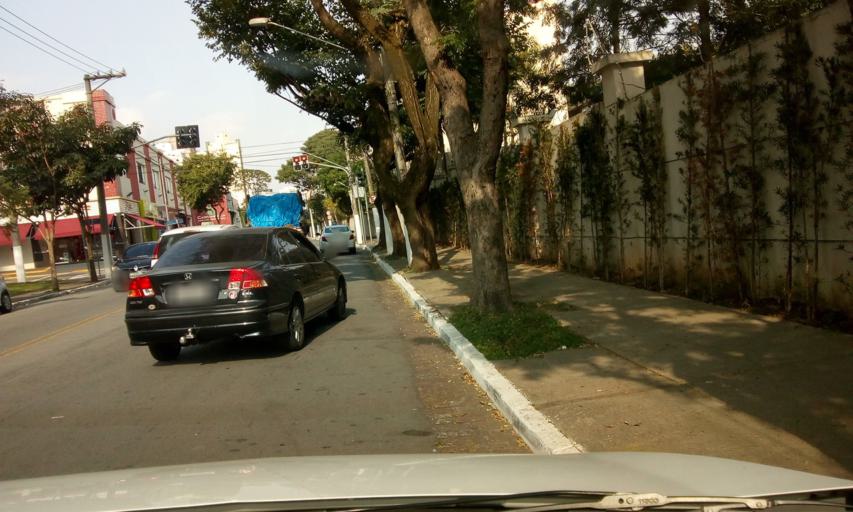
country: BR
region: Sao Paulo
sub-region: Sao Paulo
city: Sao Paulo
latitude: -23.5519
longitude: -46.5937
